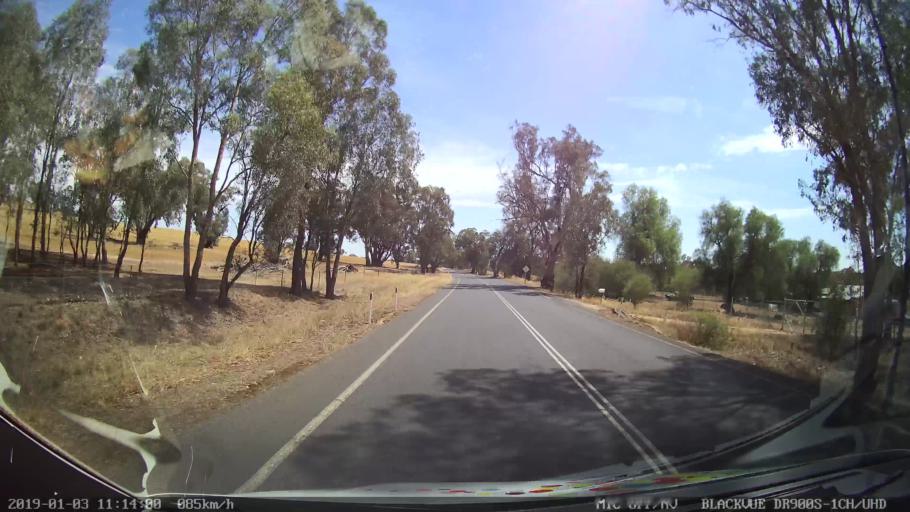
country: AU
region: New South Wales
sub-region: Young
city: Young
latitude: -34.1815
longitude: 148.2601
